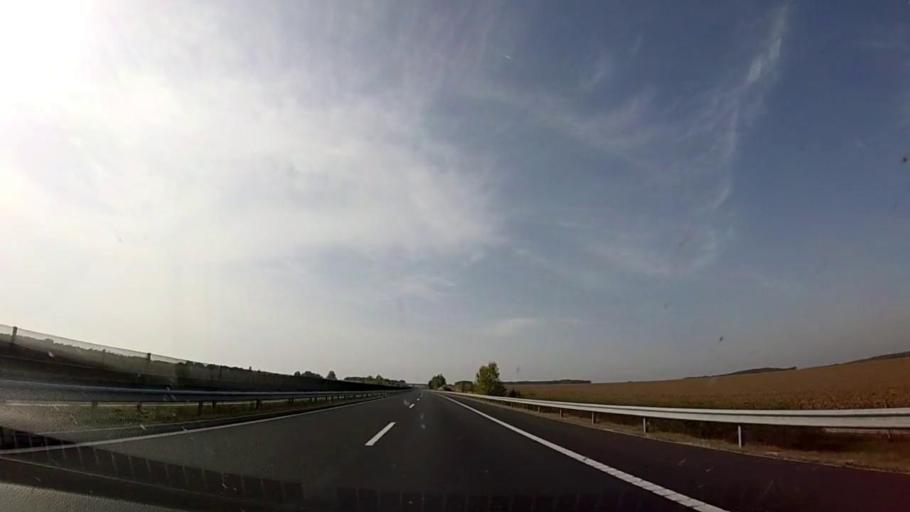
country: HU
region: Zala
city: Zalakomar
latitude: 46.4978
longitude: 17.1312
